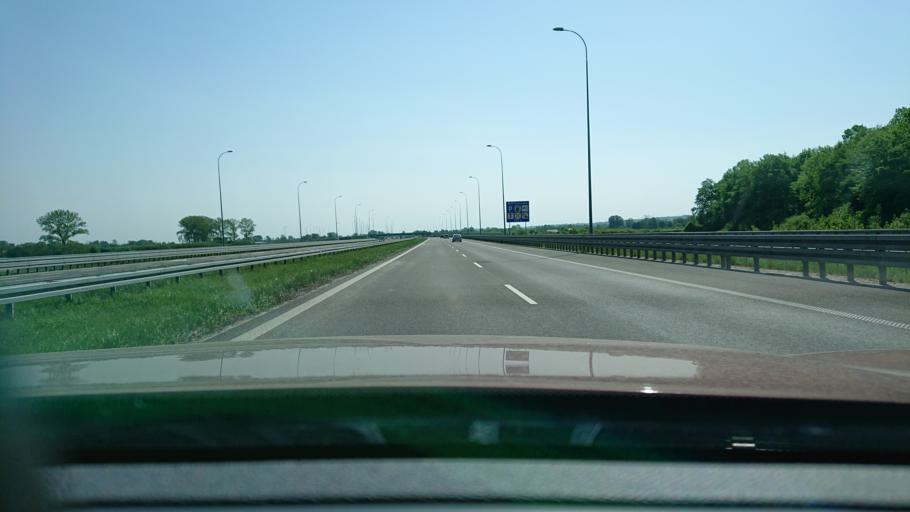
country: PL
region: Subcarpathian Voivodeship
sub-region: Powiat lancucki
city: Czarna
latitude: 50.0911
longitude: 22.1582
